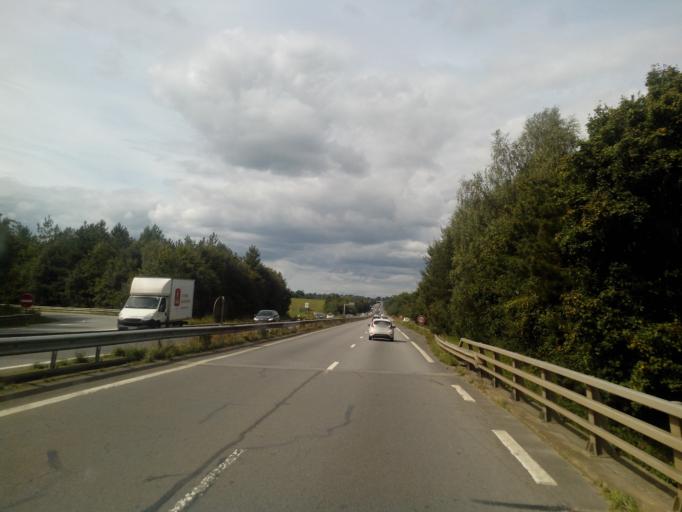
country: FR
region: Brittany
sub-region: Departement d'Ille-et-Vilaine
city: Montgermont
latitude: 48.1545
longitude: -1.7018
